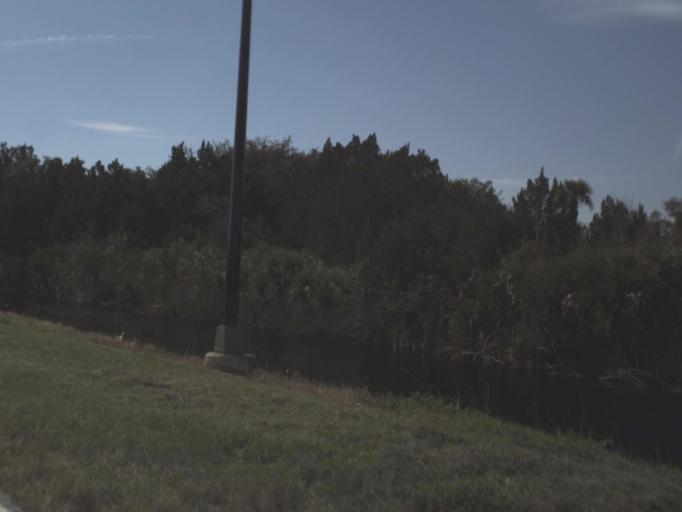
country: US
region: Florida
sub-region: Brevard County
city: Merritt Island
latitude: 28.5252
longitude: -80.6931
